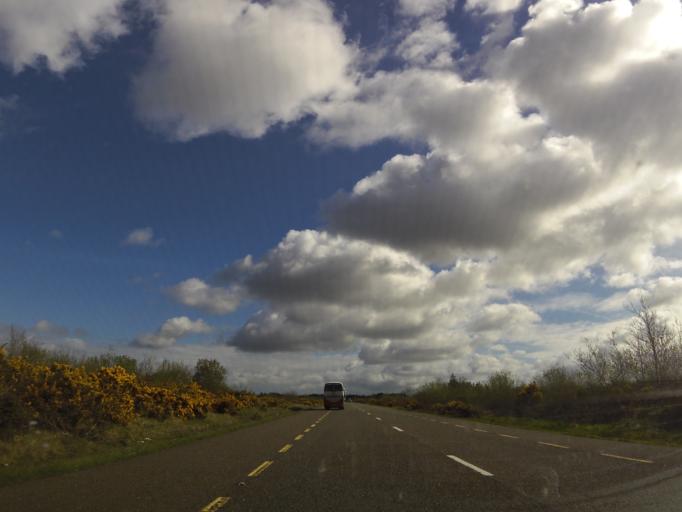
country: IE
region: Connaught
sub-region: Maigh Eo
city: Kiltamagh
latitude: 53.8040
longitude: -8.9131
